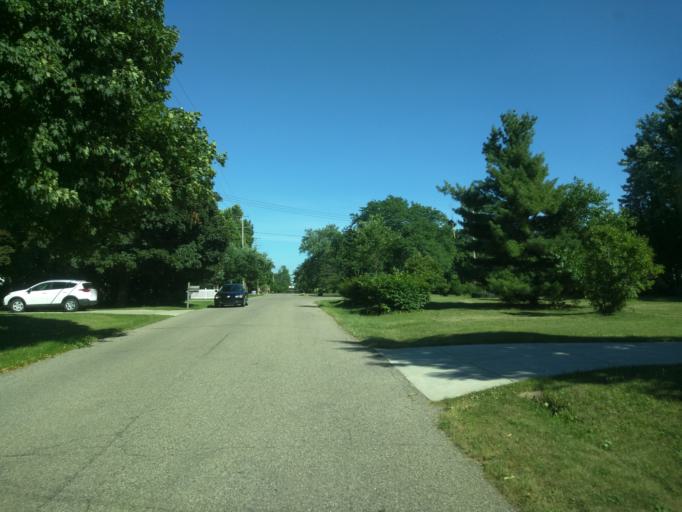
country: US
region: Michigan
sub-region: Eaton County
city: Waverly
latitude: 42.7437
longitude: -84.6411
